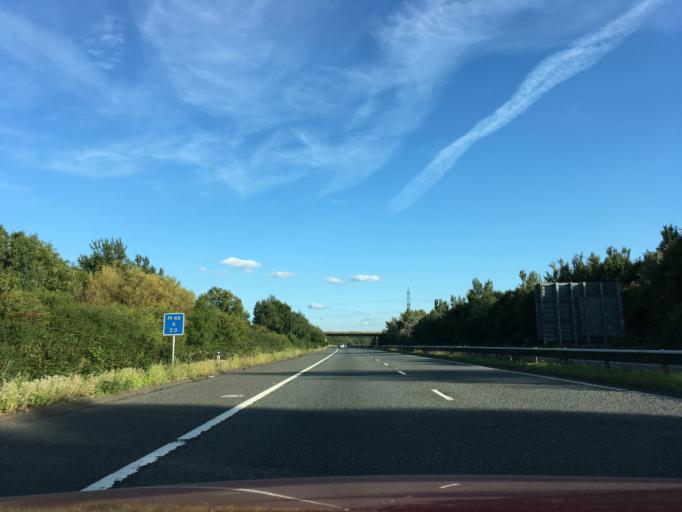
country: GB
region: England
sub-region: South Gloucestershire
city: Severn Beach
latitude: 51.5538
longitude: -2.6460
